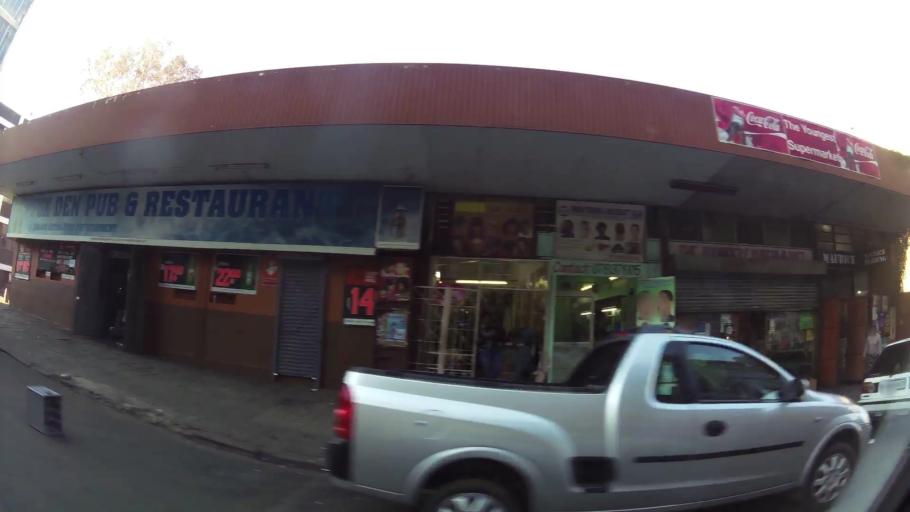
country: ZA
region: Gauteng
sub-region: City of Johannesburg Metropolitan Municipality
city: Johannesburg
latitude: -26.2048
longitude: 28.0598
